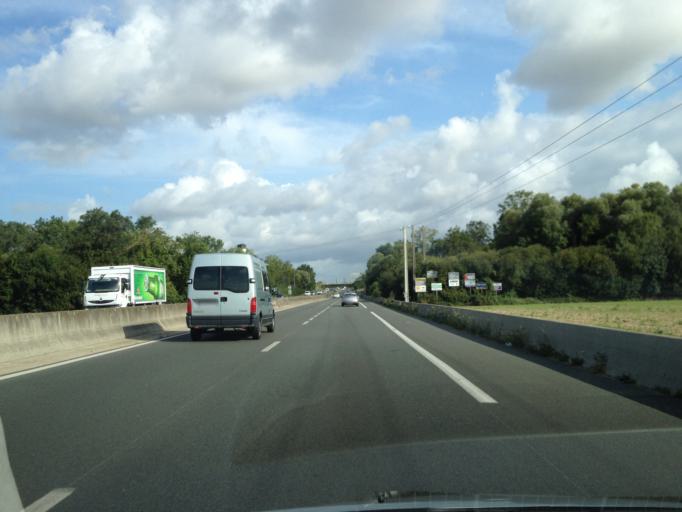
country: FR
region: Poitou-Charentes
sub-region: Departement de la Charente-Maritime
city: Aytre
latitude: 46.1473
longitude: -1.1100
